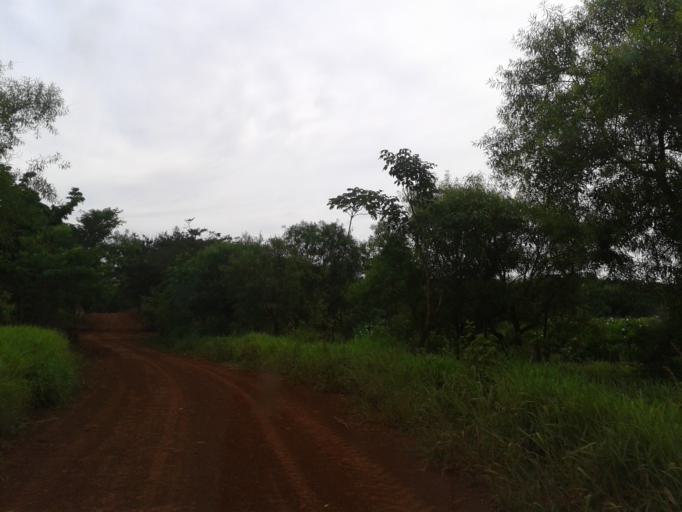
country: BR
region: Minas Gerais
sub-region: Centralina
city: Centralina
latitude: -18.6552
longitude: -49.3425
